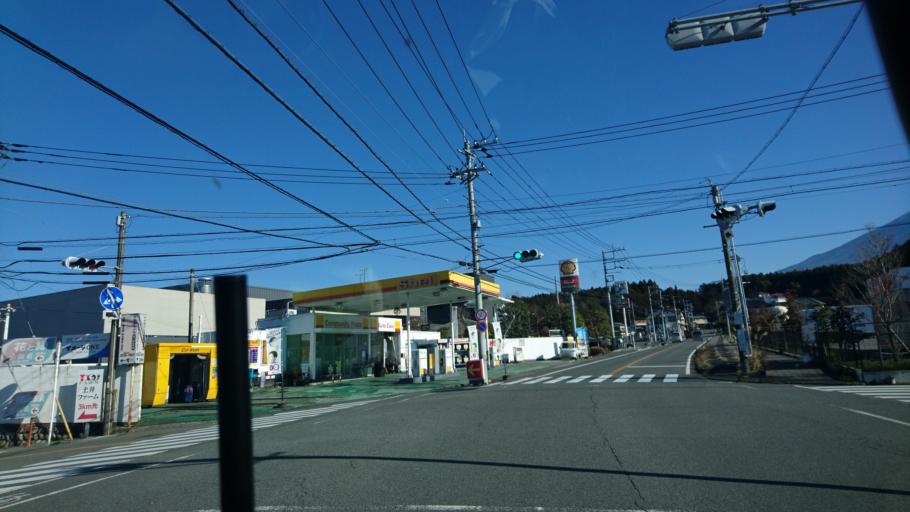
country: JP
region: Shizuoka
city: Fujinomiya
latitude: 35.2663
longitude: 138.6033
